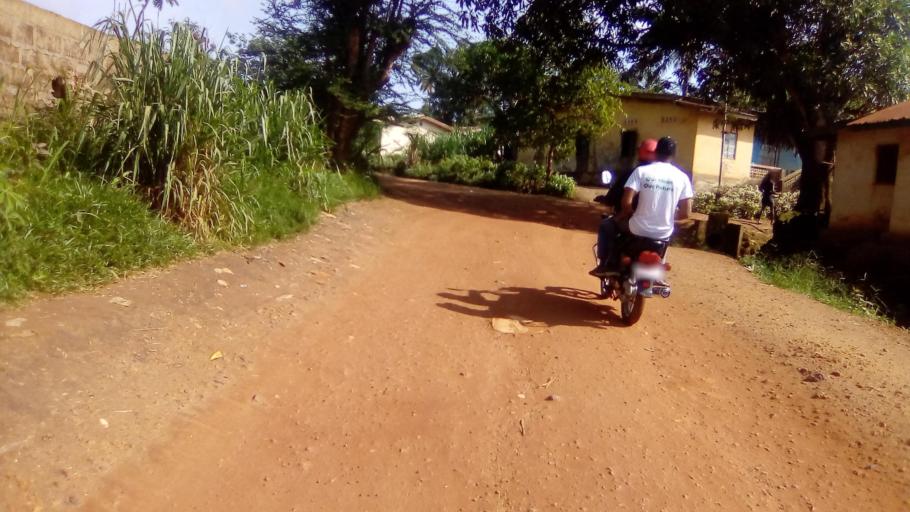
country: SL
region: Southern Province
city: Bo
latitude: 7.9713
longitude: -11.7314
